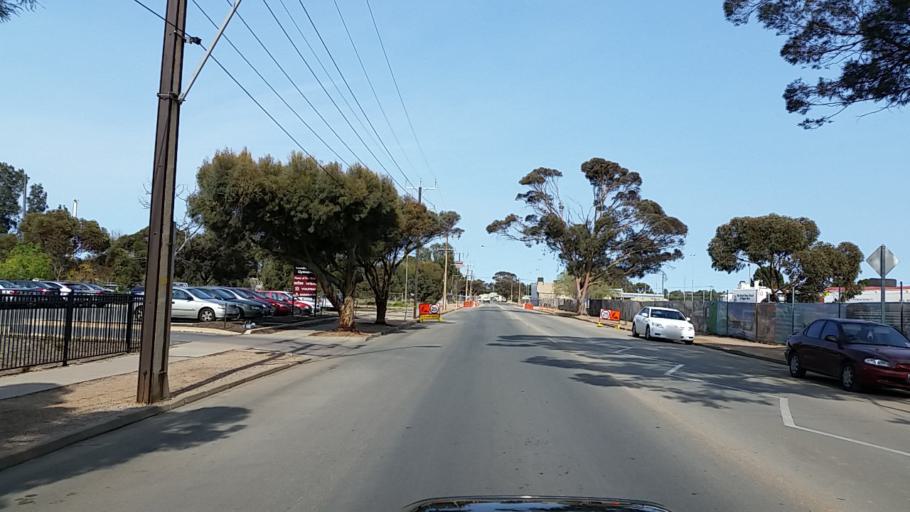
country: AU
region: South Australia
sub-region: Port Pirie City and Dists
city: Port Pirie
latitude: -33.1818
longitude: 138.0086
